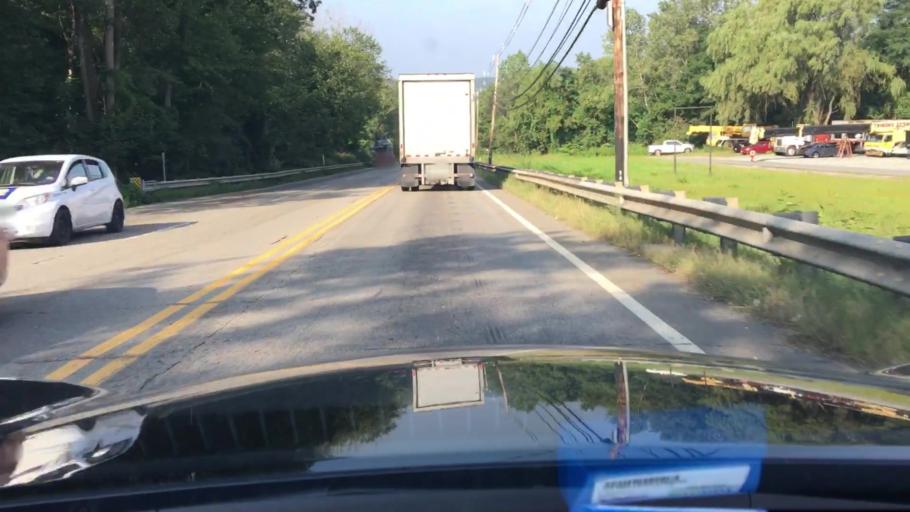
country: US
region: Massachusetts
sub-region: Worcester County
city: Hamilton
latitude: 42.2487
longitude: -71.7205
